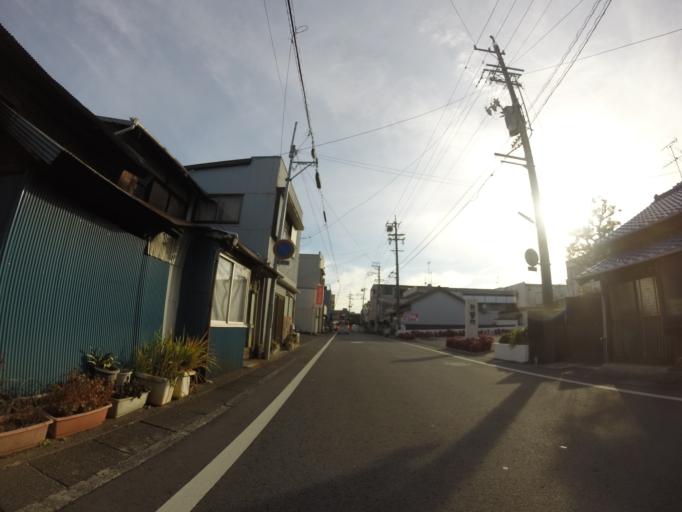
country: JP
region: Shizuoka
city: Shizuoka-shi
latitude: 35.0328
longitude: 138.4832
